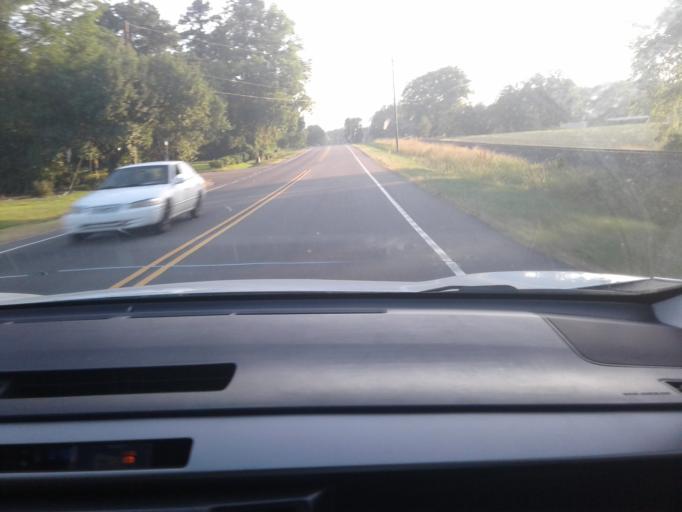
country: US
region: North Carolina
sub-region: Harnett County
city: Angier
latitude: 35.4832
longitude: -78.8189
